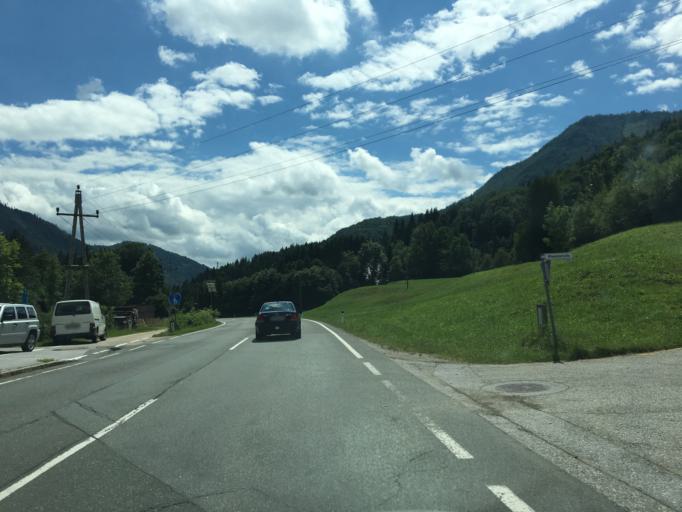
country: AT
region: Salzburg
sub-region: Politischer Bezirk Salzburg-Umgebung
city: Ebenau
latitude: 47.7764
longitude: 13.1810
